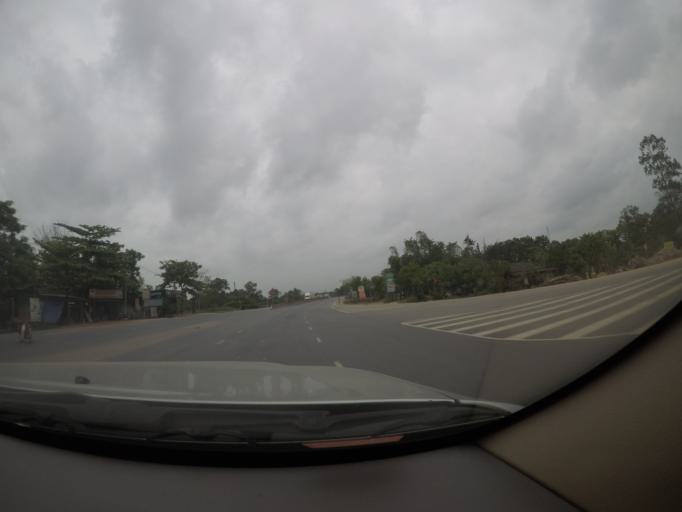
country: VN
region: Quang Tri
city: Hai Lang
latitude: 16.7162
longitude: 107.2127
